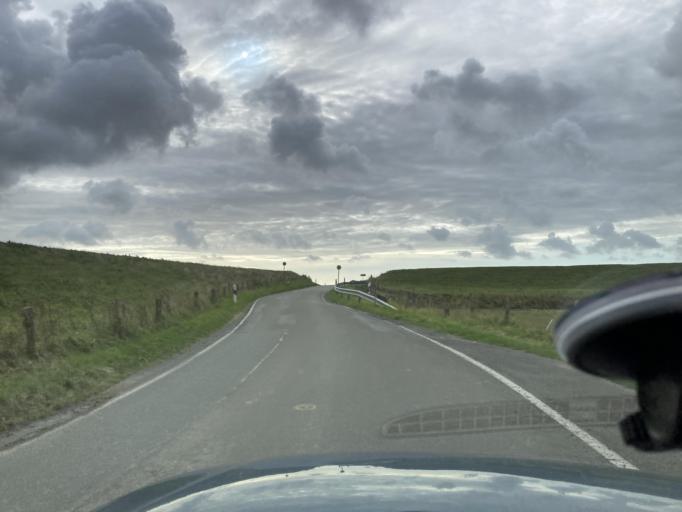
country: DE
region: Schleswig-Holstein
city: Schulp
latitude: 54.2646
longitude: 8.9307
